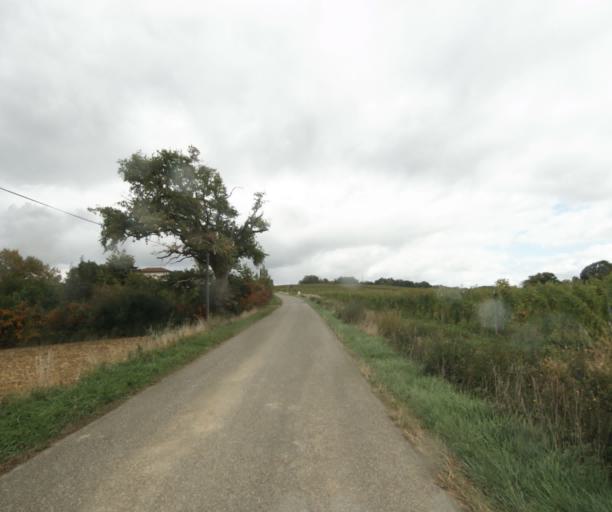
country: FR
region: Midi-Pyrenees
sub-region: Departement du Gers
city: Nogaro
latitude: 43.8244
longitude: -0.0408
